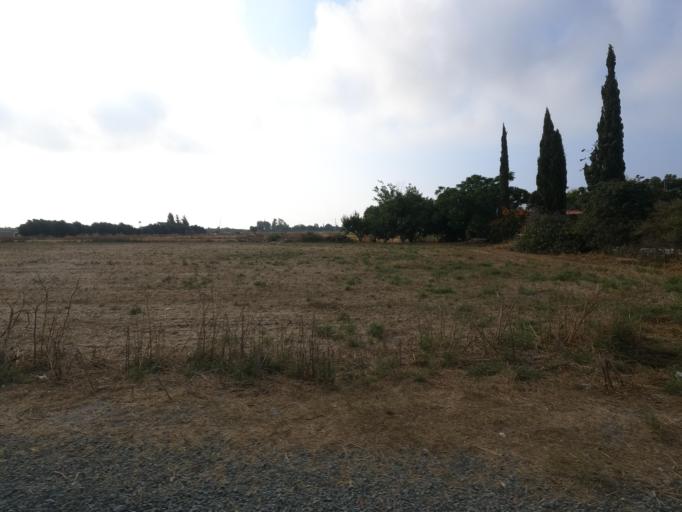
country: CY
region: Larnaka
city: Kiti
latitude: 34.8300
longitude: 33.5552
